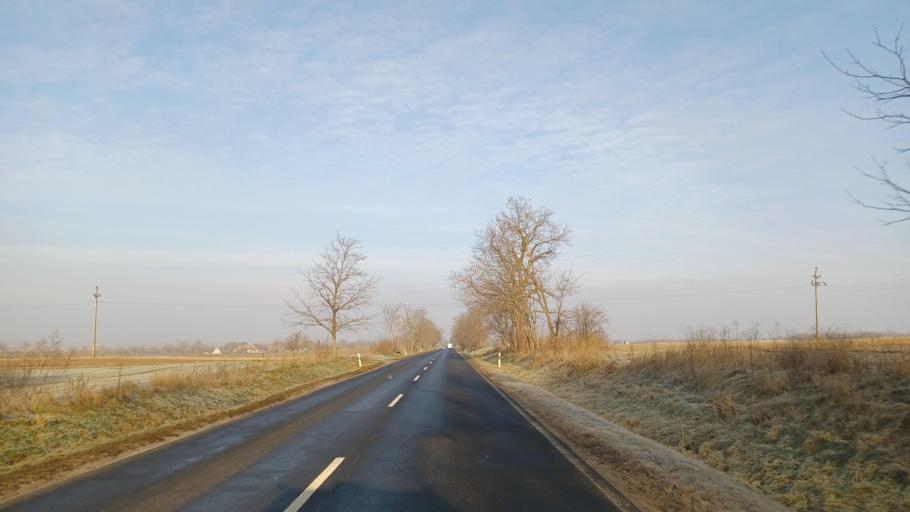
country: HU
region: Fejer
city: Cece
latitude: 46.7494
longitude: 18.6434
